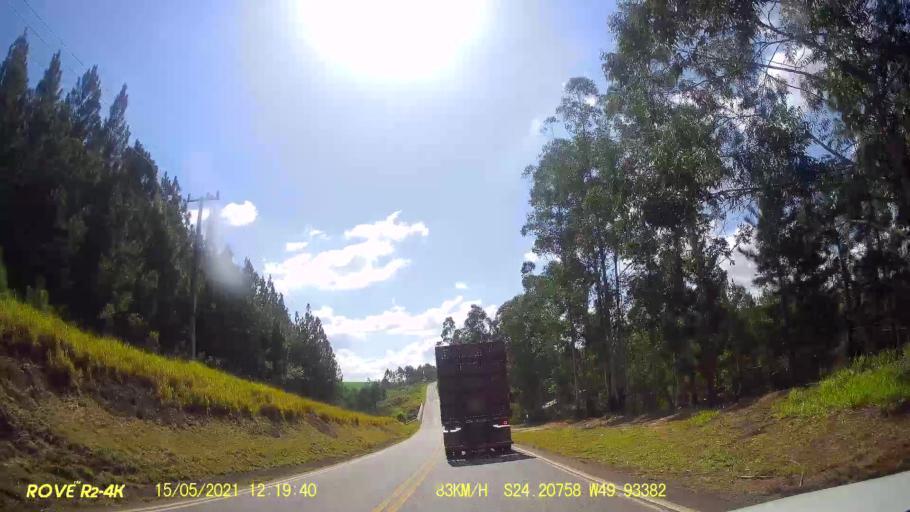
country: BR
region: Parana
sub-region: Jaguariaiva
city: Jaguariaiva
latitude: -24.2072
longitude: -49.9336
